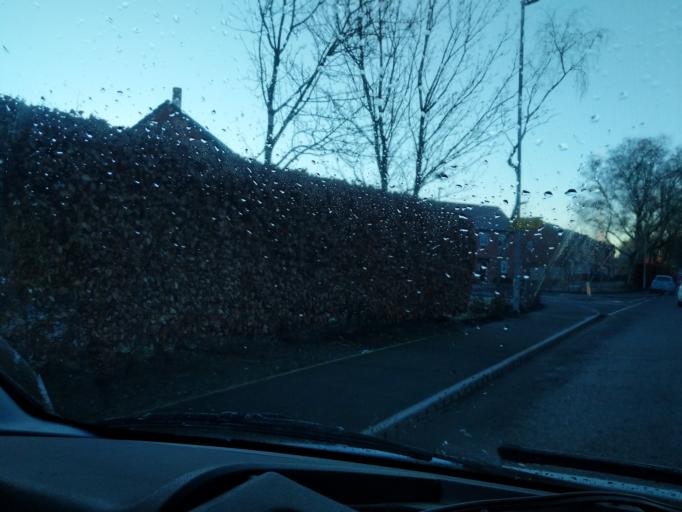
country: GB
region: England
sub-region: St. Helens
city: St Helens
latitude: 53.4672
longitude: -2.7426
